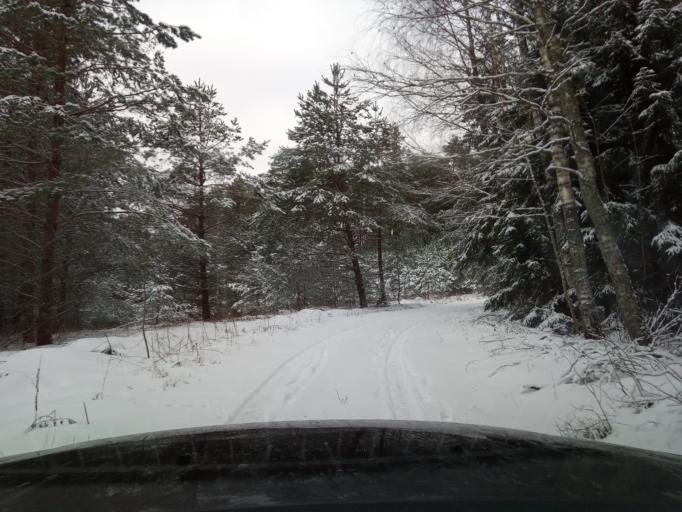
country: LT
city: Zarasai
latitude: 55.6751
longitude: 26.0277
